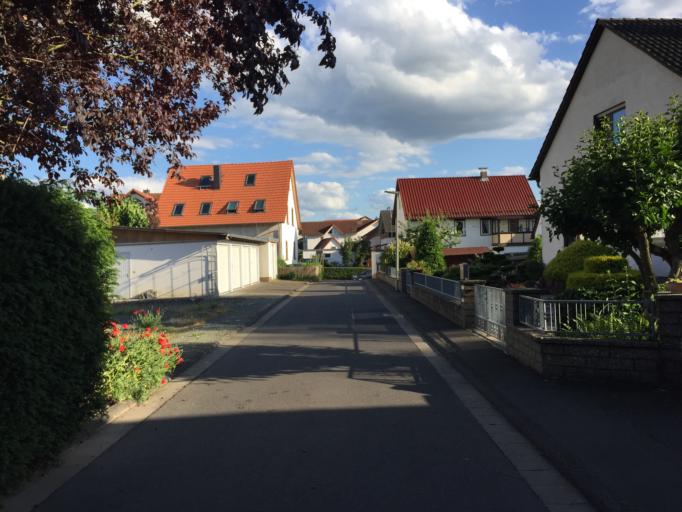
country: DE
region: Hesse
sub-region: Regierungsbezirk Darmstadt
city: Karben
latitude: 50.2244
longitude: 8.7771
